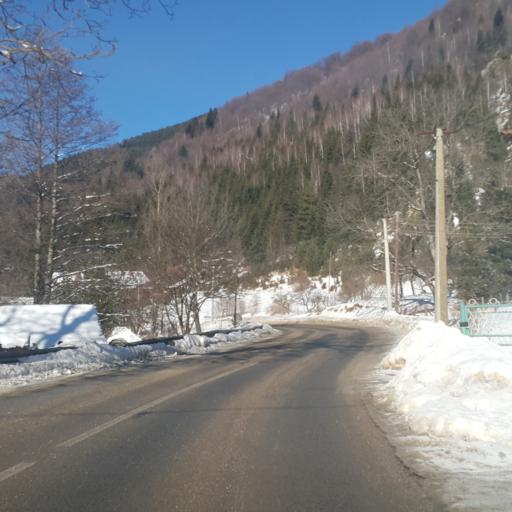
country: XK
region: Mitrovica
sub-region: Komuna e Leposaviqit
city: Leposaviq
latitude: 43.3049
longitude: 20.8748
